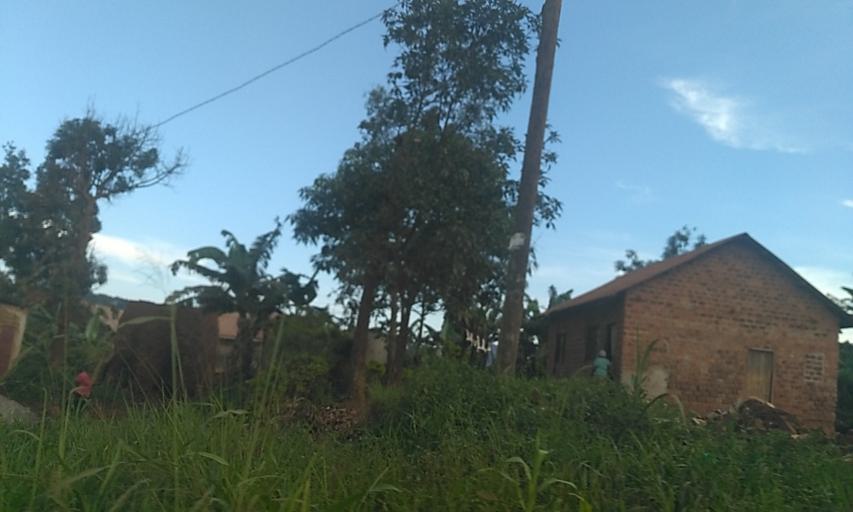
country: UG
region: Central Region
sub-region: Wakiso District
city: Kajansi
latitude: 0.2406
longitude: 32.4968
